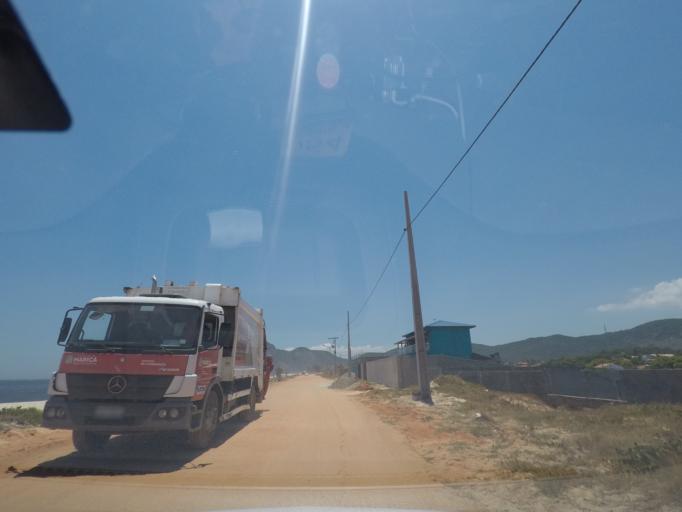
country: BR
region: Rio de Janeiro
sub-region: Niteroi
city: Niteroi
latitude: -22.9693
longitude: -42.9736
